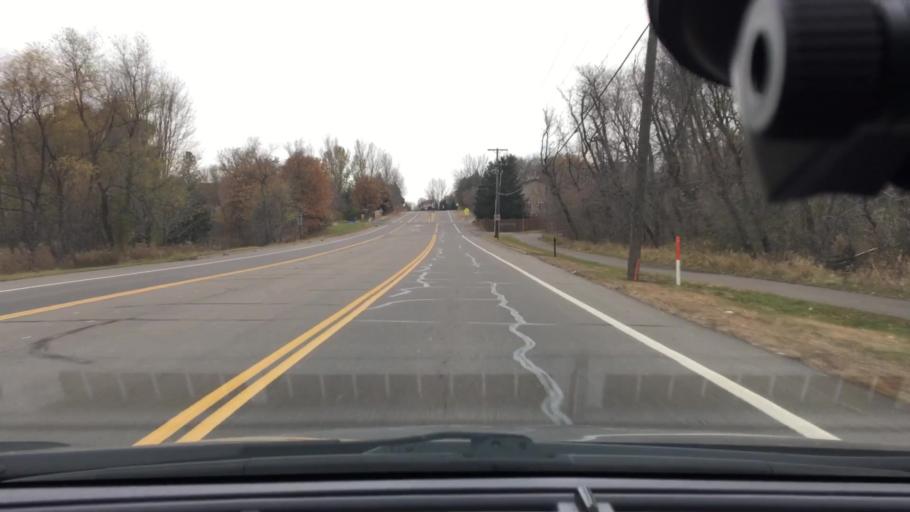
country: US
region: Minnesota
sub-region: Hennepin County
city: Corcoran
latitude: 45.1098
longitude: -93.5117
